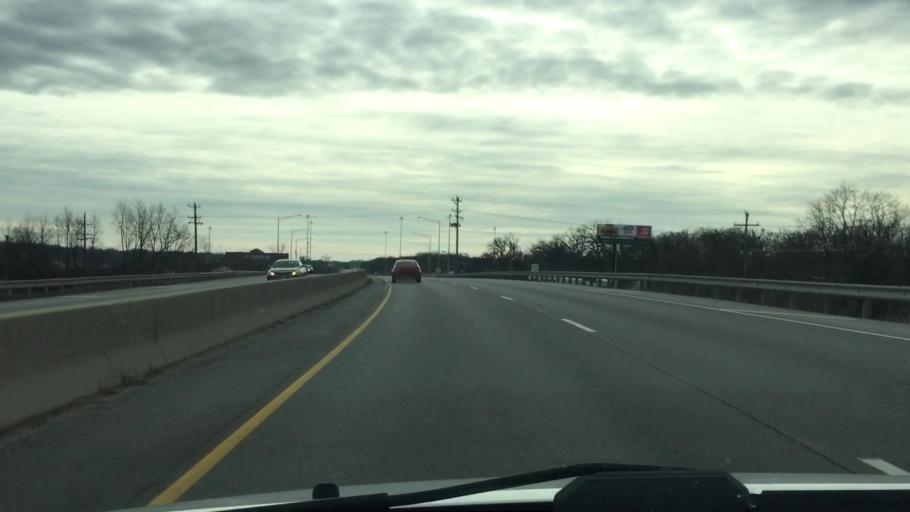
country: US
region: Illinois
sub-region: McHenry County
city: Crystal Lake
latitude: 42.2307
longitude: -88.2880
